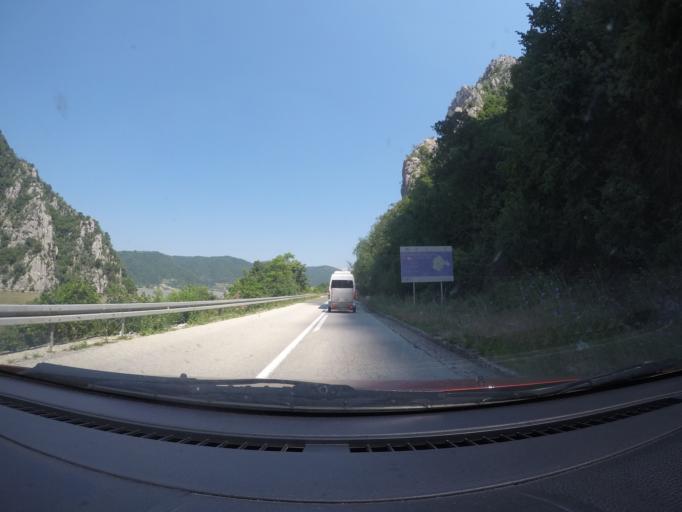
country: RO
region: Mehedinti
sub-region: Comuna Dubova
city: Dubova
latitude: 44.6147
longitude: 22.2752
